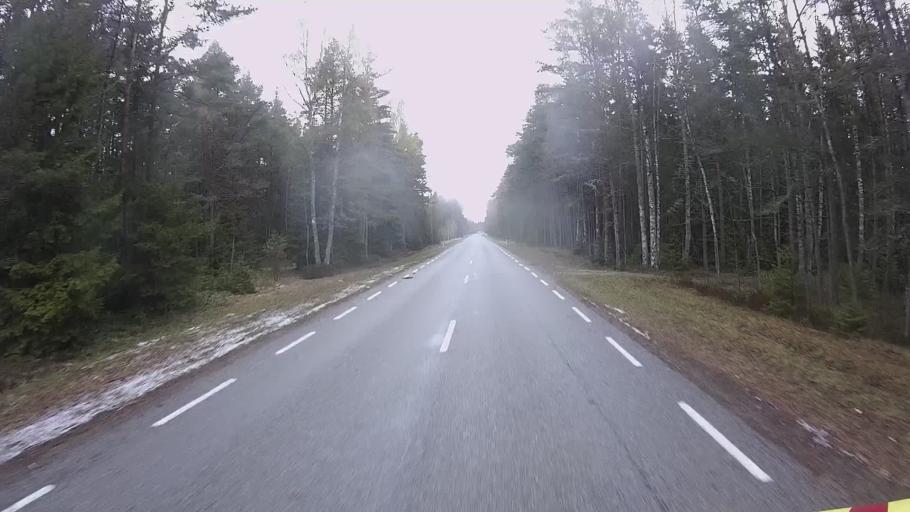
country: EE
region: Hiiumaa
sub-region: Kaerdla linn
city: Kardla
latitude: 59.0622
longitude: 22.6854
